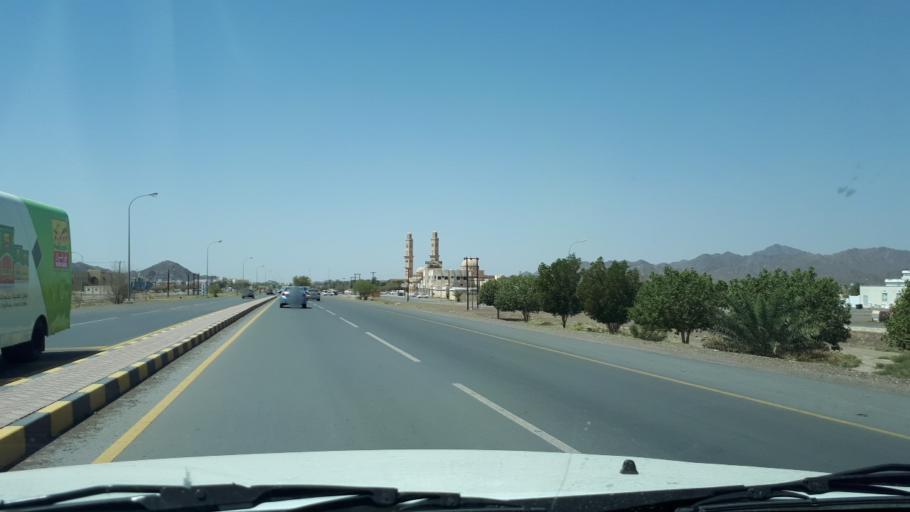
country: OM
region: Muhafazat ad Dakhiliyah
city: Bahla'
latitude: 22.9978
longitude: 57.3164
